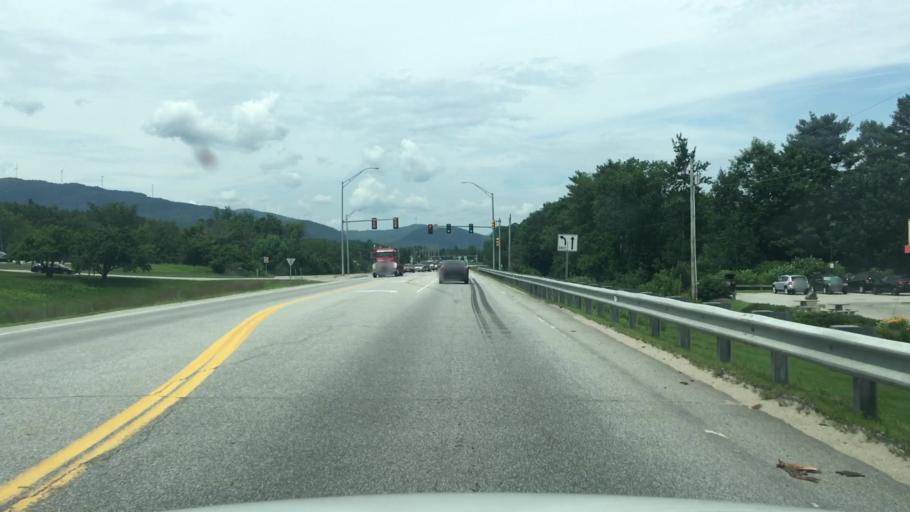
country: US
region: New Hampshire
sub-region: Grafton County
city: Plymouth
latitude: 43.7699
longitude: -71.7148
